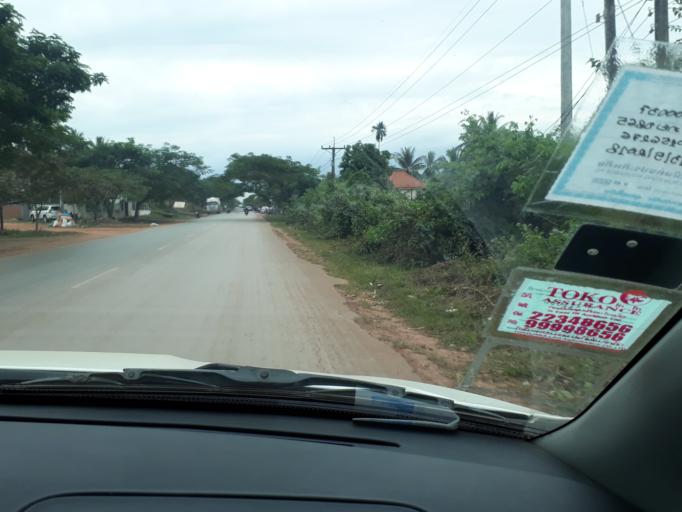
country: LA
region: Vientiane
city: Muang Phon-Hong
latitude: 18.3307
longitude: 102.4425
